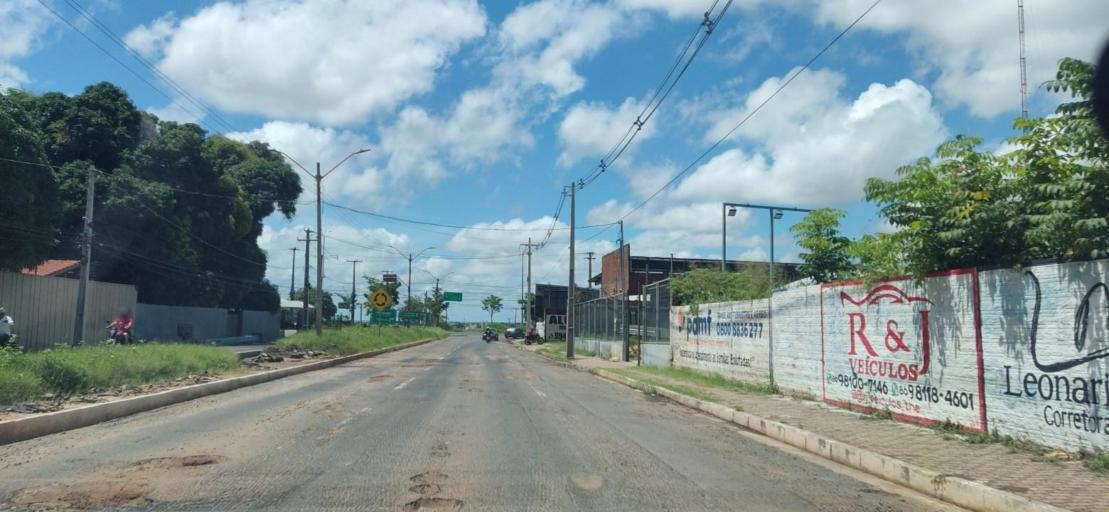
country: BR
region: Piaui
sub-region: Teresina
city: Teresina
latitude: -5.0770
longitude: -42.7497
